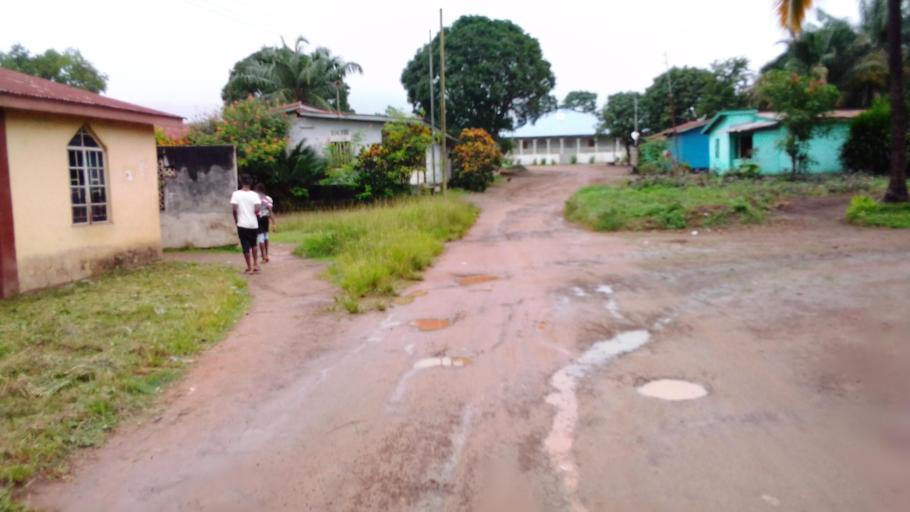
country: SL
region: Eastern Province
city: Kenema
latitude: 7.8987
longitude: -11.1697
